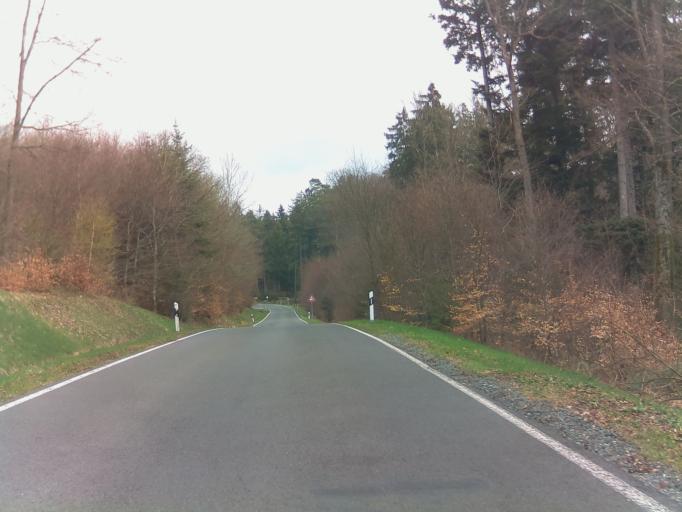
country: DE
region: Rheinland-Pfalz
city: Bruchweiler
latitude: 49.8067
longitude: 7.2203
